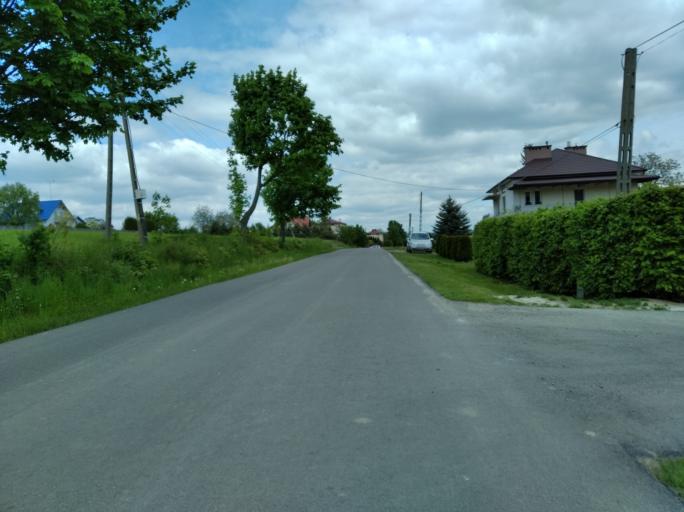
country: PL
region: Subcarpathian Voivodeship
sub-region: Powiat ropczycko-sedziszowski
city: Wielopole Skrzynskie
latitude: 49.9354
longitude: 21.6021
